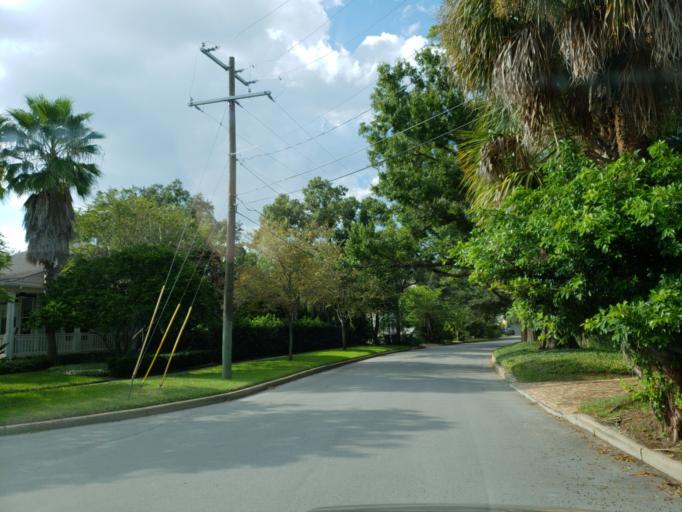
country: US
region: Florida
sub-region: Hillsborough County
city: Tampa
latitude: 27.9258
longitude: -82.4590
